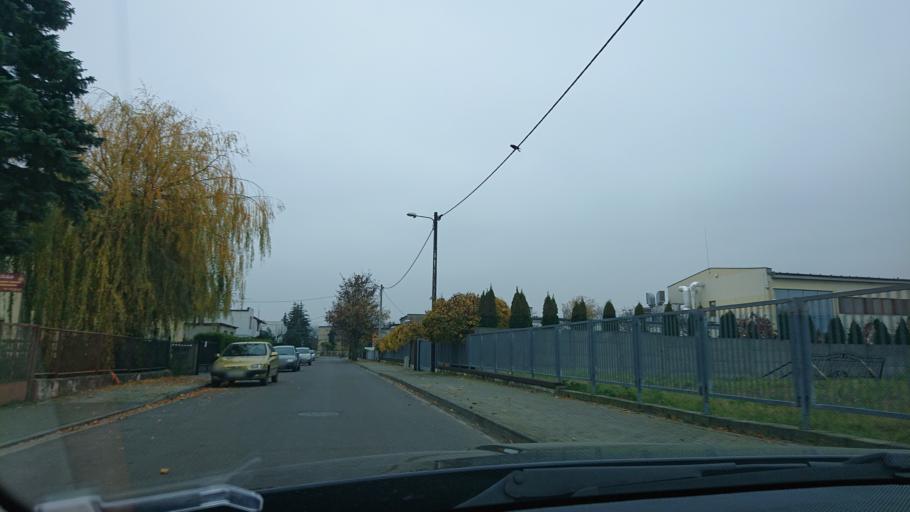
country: PL
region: Greater Poland Voivodeship
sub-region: Powiat gnieznienski
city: Gniezno
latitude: 52.5373
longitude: 17.6242
